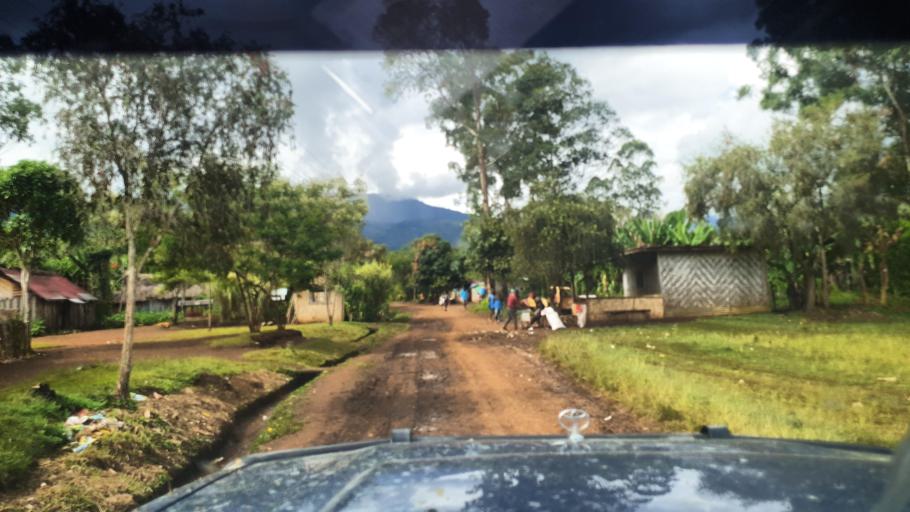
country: PG
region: Jiwaka
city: Minj
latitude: -5.8994
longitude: 144.8112
